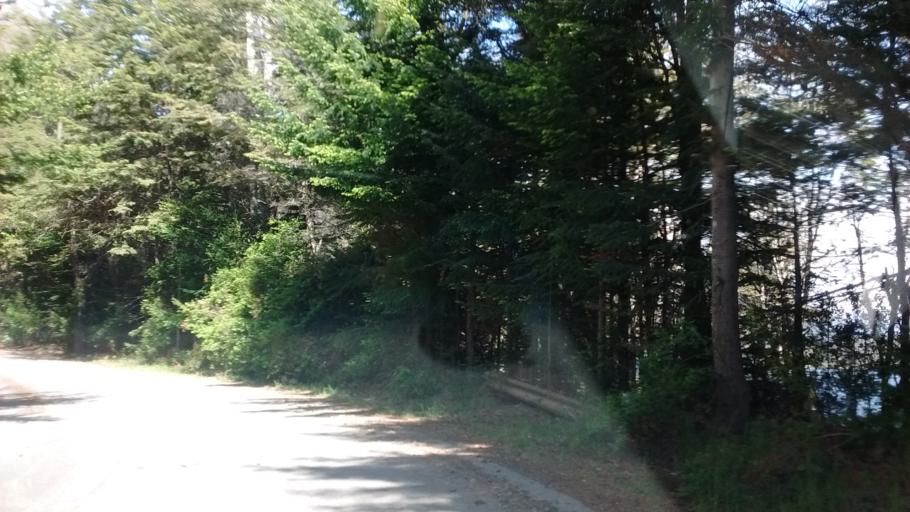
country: AR
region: Rio Negro
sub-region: Departamento de Bariloche
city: San Carlos de Bariloche
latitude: -41.0708
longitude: -71.5431
